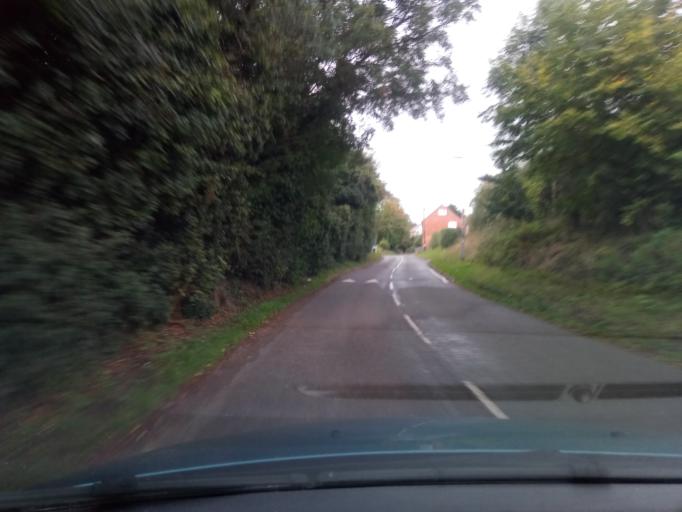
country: GB
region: England
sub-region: Leicestershire
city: Sileby
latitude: 52.7514
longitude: -1.0818
